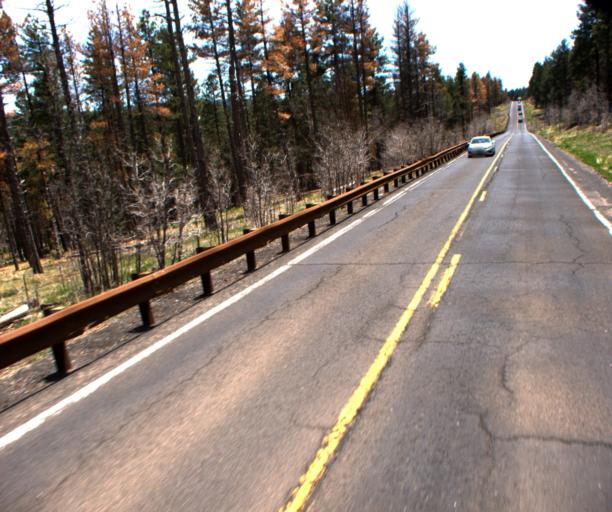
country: US
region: Arizona
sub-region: Coconino County
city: Kachina Village
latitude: 35.0518
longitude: -111.7328
